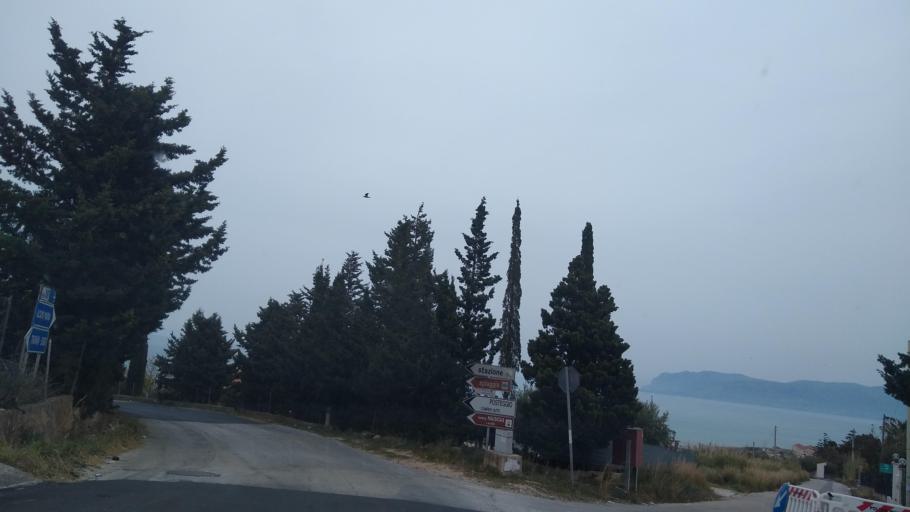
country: IT
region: Sicily
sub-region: Trapani
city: Castellammare del Golfo
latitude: 38.0194
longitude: 12.8983
